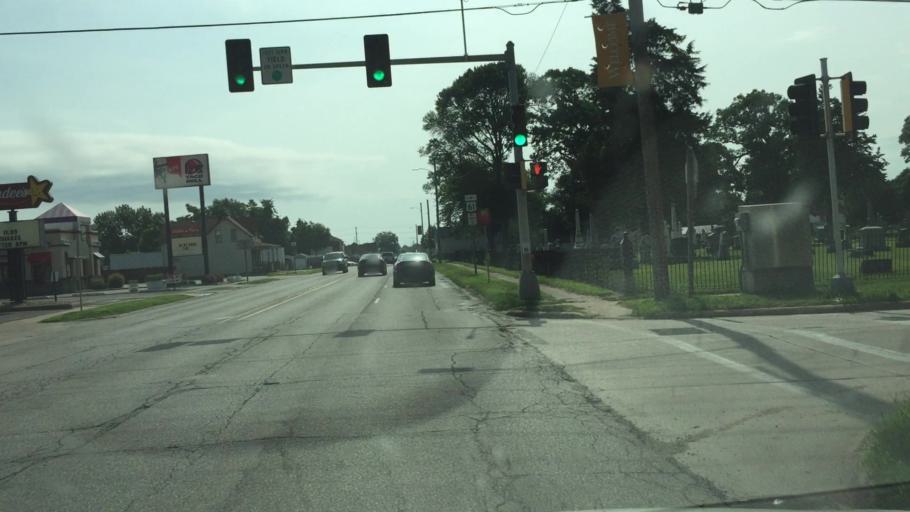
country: US
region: Iowa
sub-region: Lee County
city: Fort Madison
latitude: 40.6301
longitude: -91.3247
